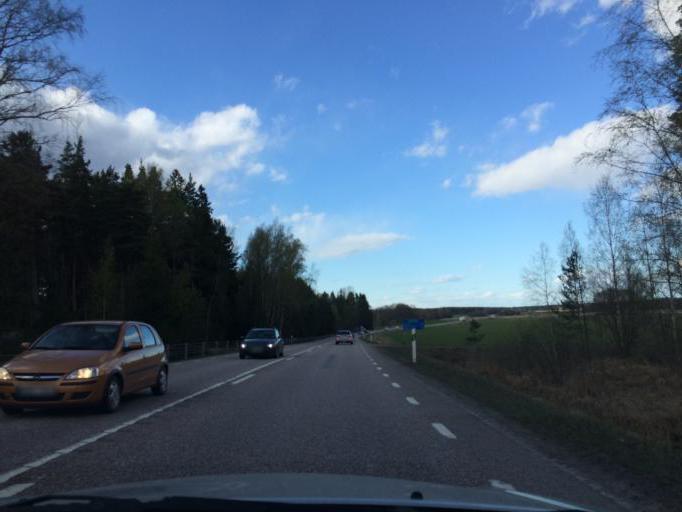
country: SE
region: Vaestmanland
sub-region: Hallstahammars Kommun
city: Kolback
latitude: 59.5331
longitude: 16.3205
